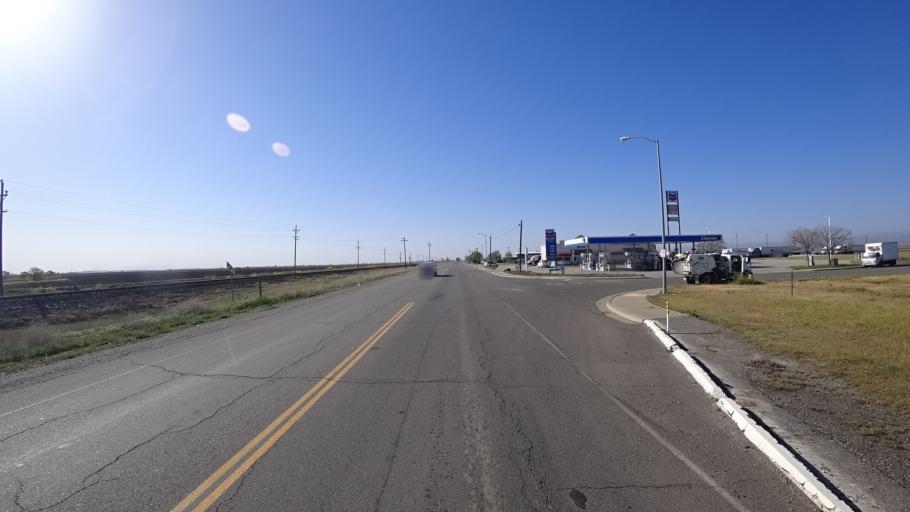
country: US
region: California
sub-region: Glenn County
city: Willows
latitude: 39.4945
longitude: -122.1933
